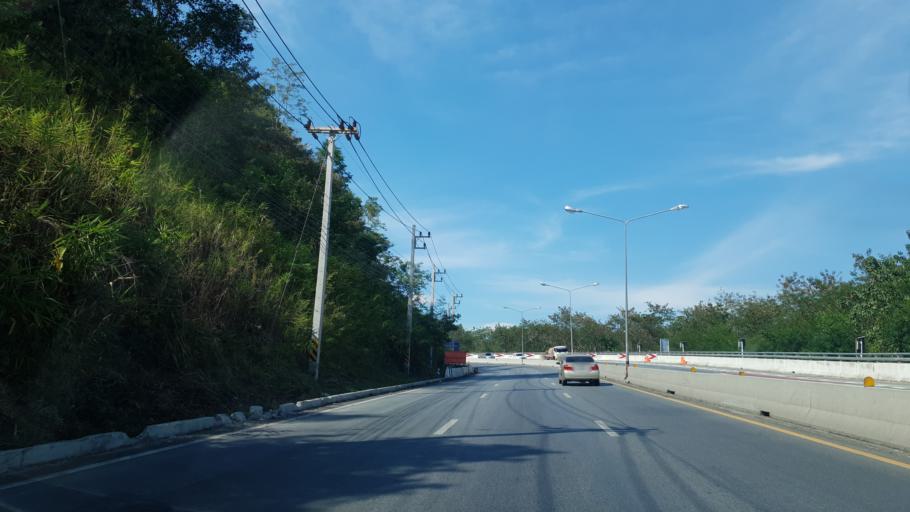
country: TH
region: Phrae
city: Den Chai
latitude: 17.8289
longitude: 100.0642
